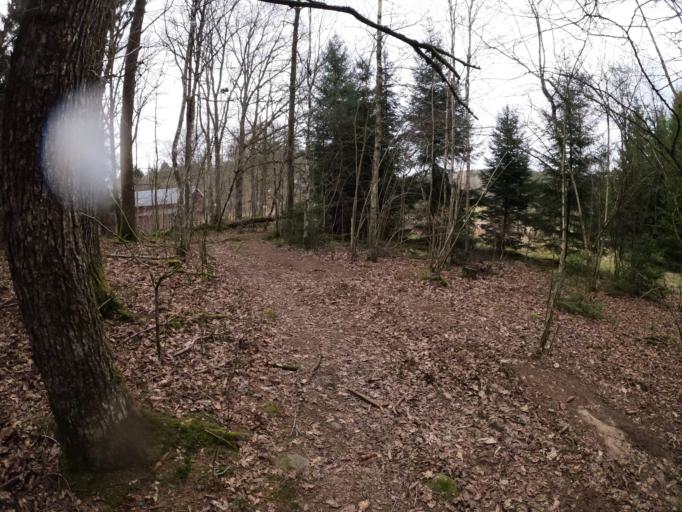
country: SE
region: Vaestra Goetaland
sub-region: Harryda Kommun
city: Molnlycke
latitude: 57.6239
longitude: 12.1071
